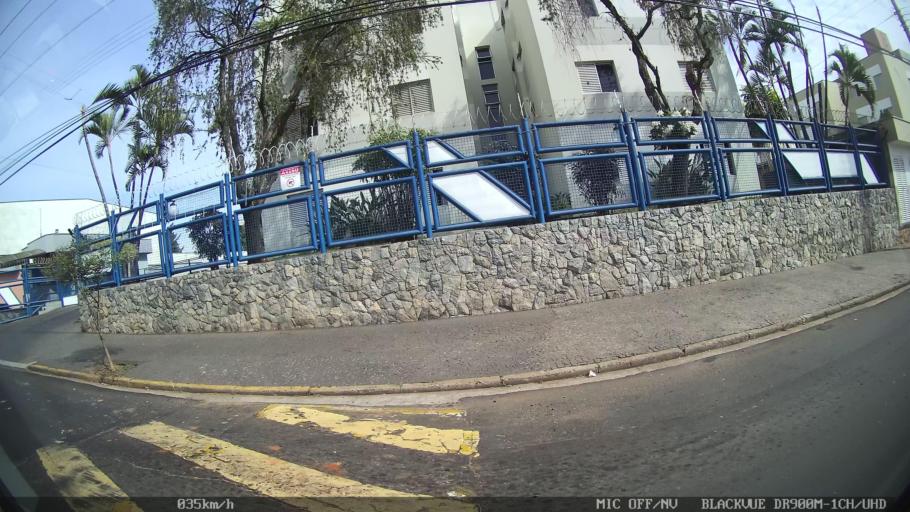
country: BR
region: Sao Paulo
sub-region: Piracicaba
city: Piracicaba
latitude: -22.7484
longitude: -47.6378
